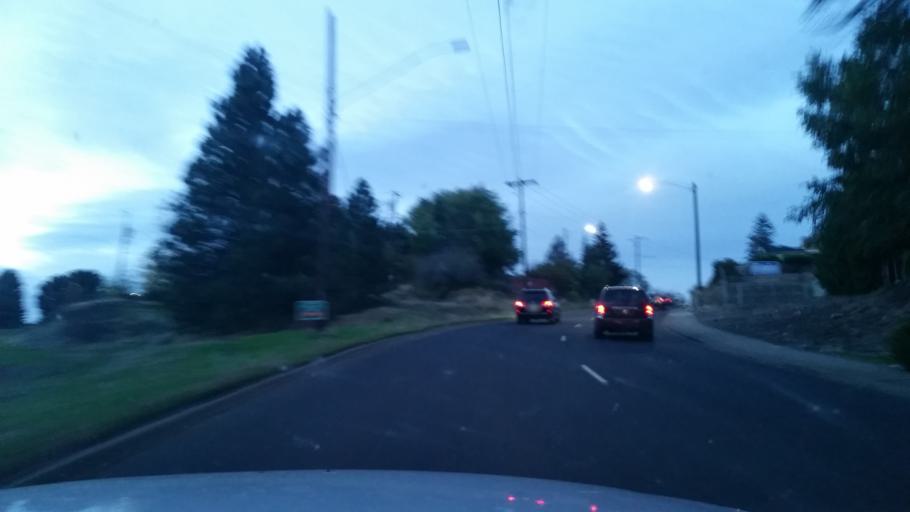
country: US
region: Washington
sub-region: Spokane County
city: Spokane
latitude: 47.6881
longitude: -117.4352
